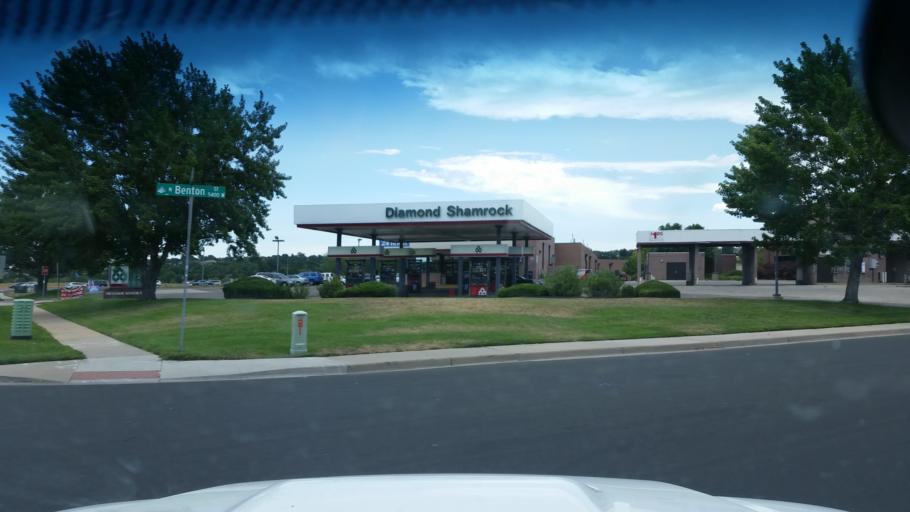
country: US
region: Colorado
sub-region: Broomfield County
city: Broomfield
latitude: 39.8997
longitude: -105.0552
